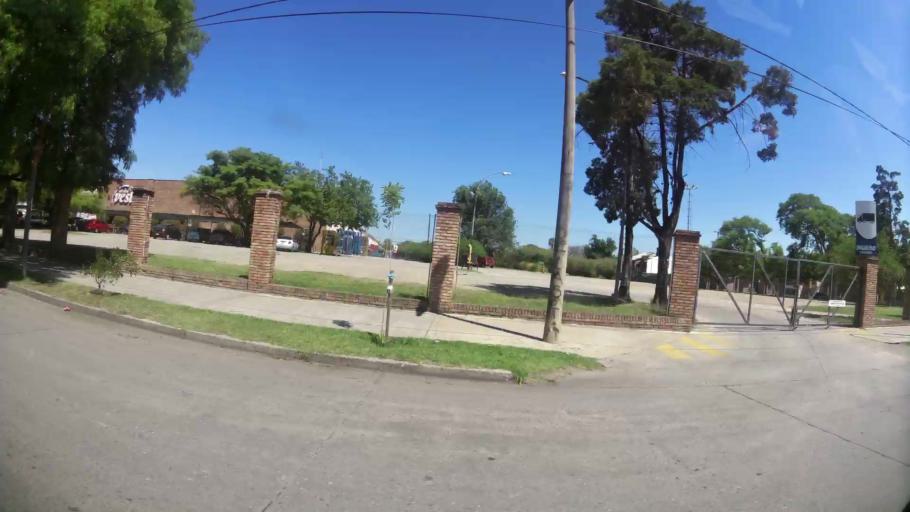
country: AR
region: Cordoba
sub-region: Departamento de Capital
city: Cordoba
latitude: -31.4280
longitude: -64.2105
